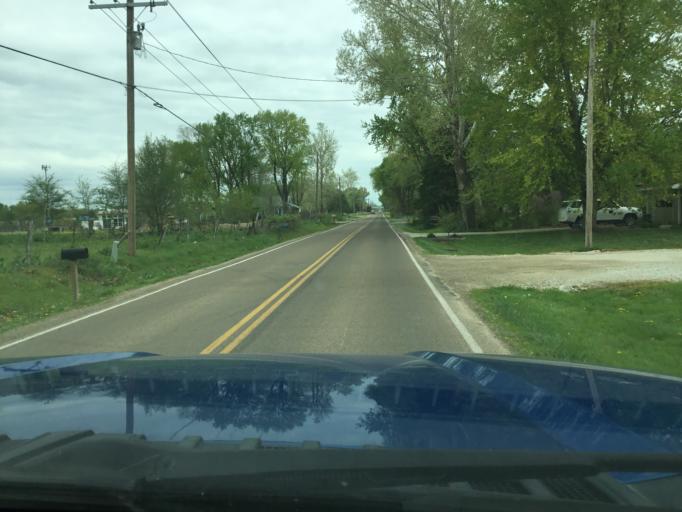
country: US
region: Kansas
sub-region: Douglas County
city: Lawrence
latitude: 38.9864
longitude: -95.2240
